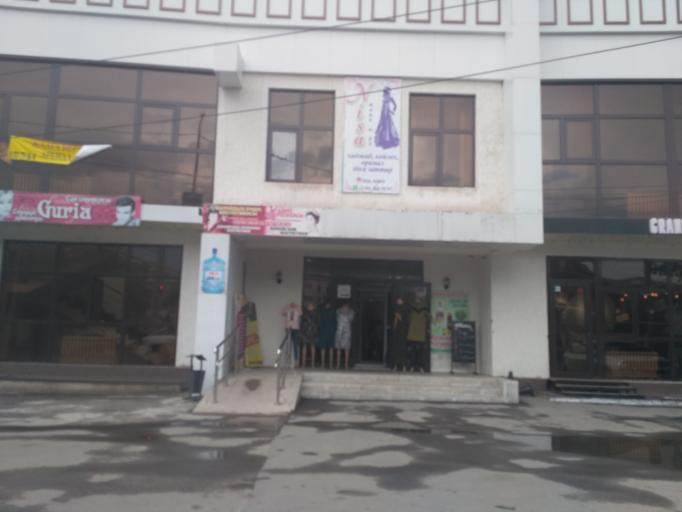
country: KZ
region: Almaty Oblysy
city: Burunday
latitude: 43.2038
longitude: 76.6167
